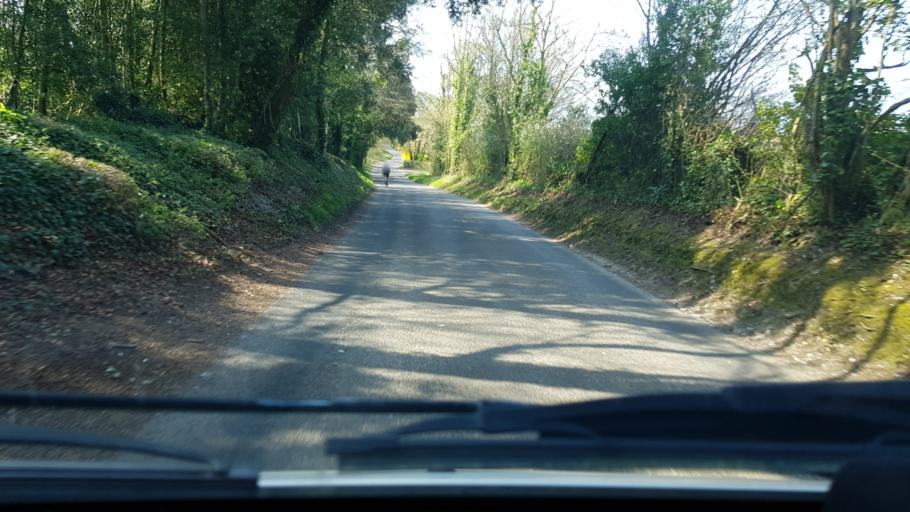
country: GB
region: England
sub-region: West Sussex
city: Chichester
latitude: 50.8750
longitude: -0.7574
